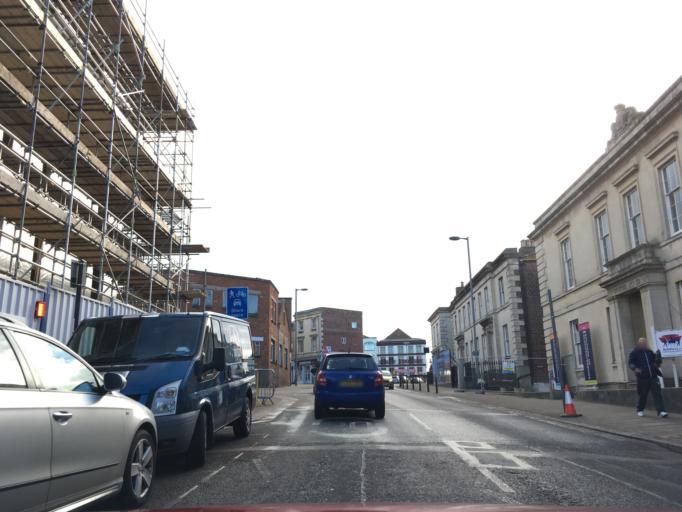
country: GB
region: England
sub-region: Gloucestershire
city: Gloucester
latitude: 51.8641
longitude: -2.2501
